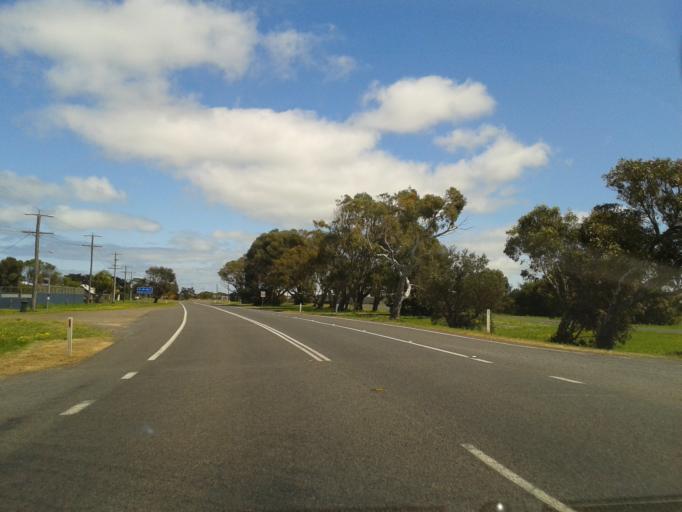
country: AU
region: Victoria
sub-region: Moyne
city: Port Fairy
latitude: -38.3164
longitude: 142.0680
